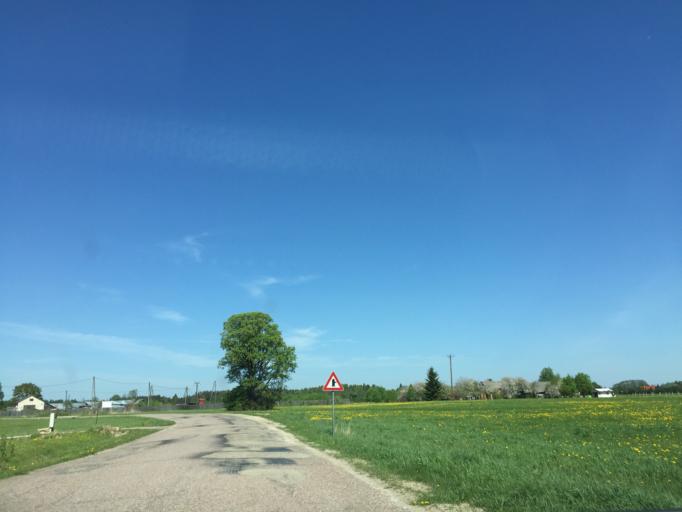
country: LV
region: Ogre
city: Ogre
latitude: 56.8555
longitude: 24.7034
